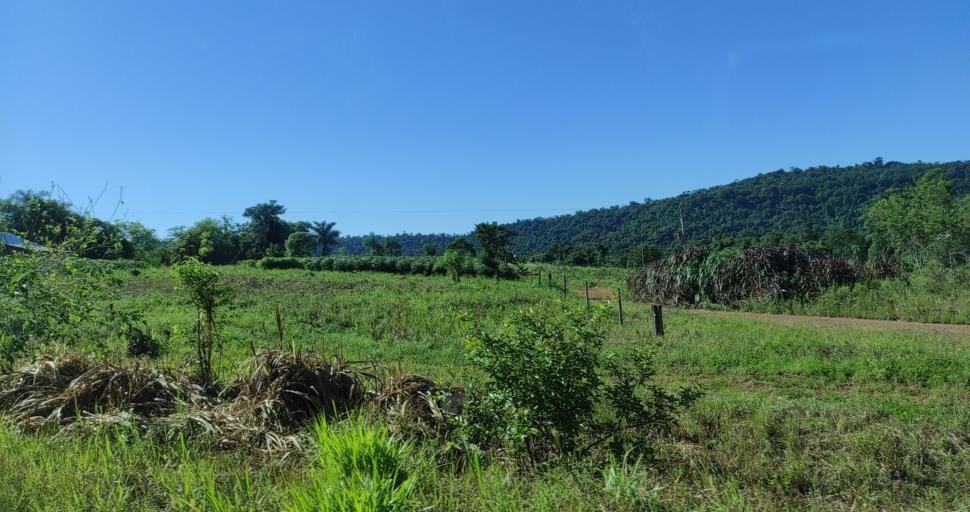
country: AR
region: Misiones
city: El Soberbio
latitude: -27.2473
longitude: -54.0315
